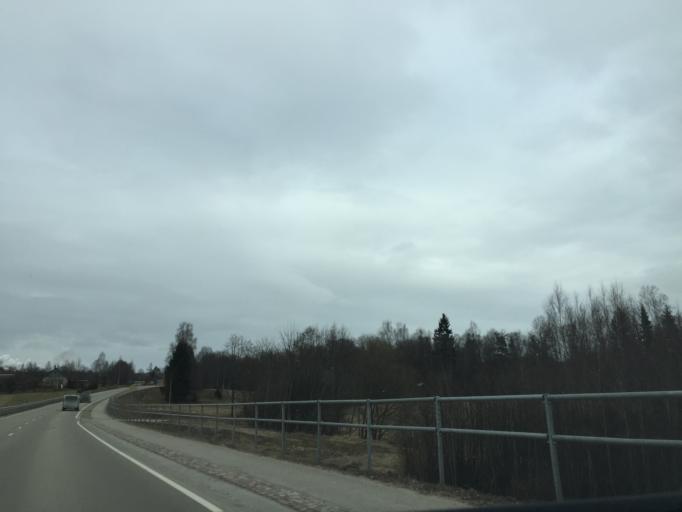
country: LV
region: Kraslavas Rajons
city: Kraslava
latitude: 55.9170
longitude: 27.1511
